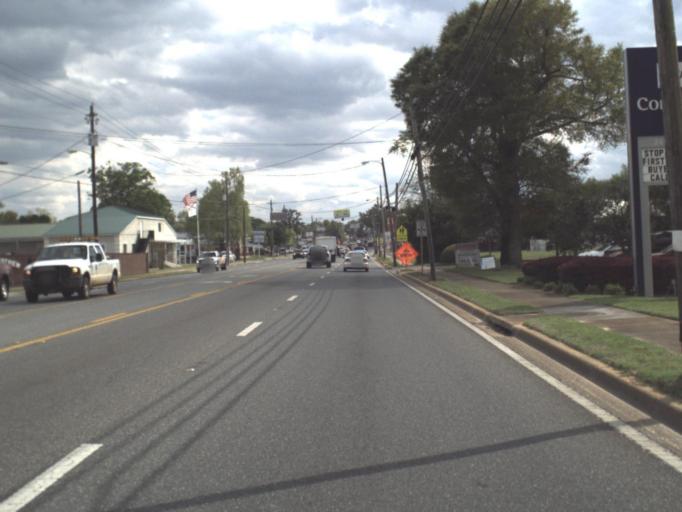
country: US
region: Florida
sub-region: Okaloosa County
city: Crestview
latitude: 30.7711
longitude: -86.5660
